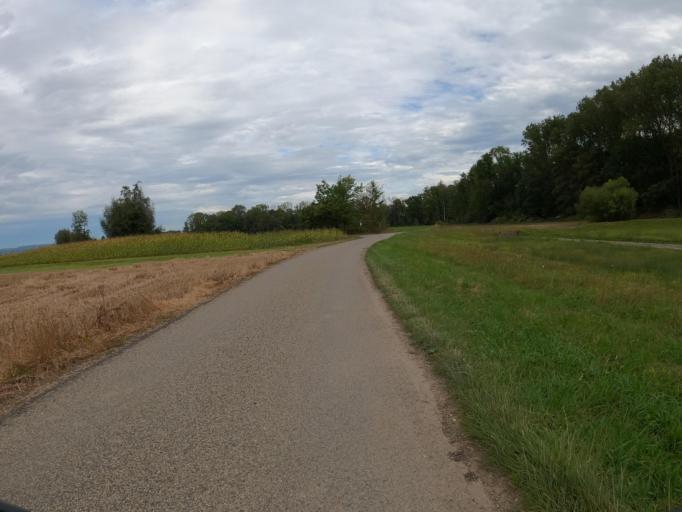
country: DE
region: Bavaria
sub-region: Swabia
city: Holzheim
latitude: 48.3903
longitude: 10.0765
